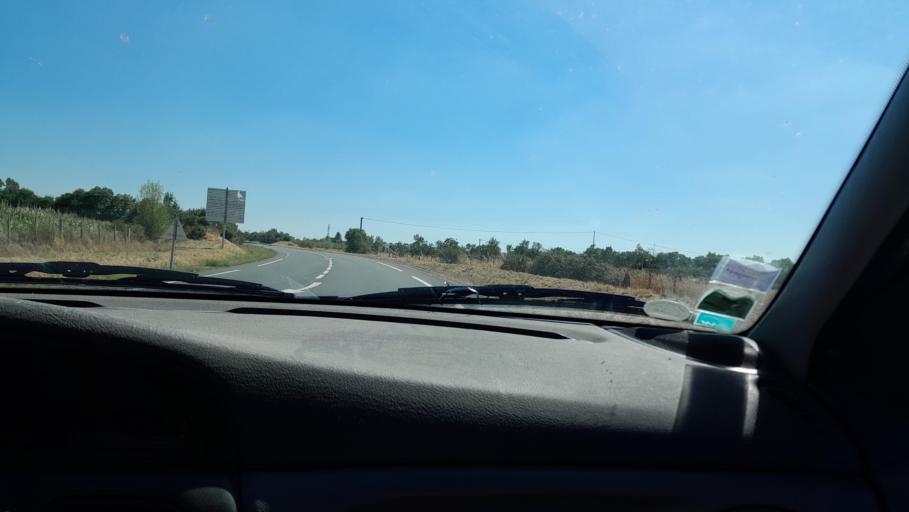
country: FR
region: Pays de la Loire
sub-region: Departement de la Loire-Atlantique
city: Saint-Gereon
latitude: 47.3794
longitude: -1.2111
